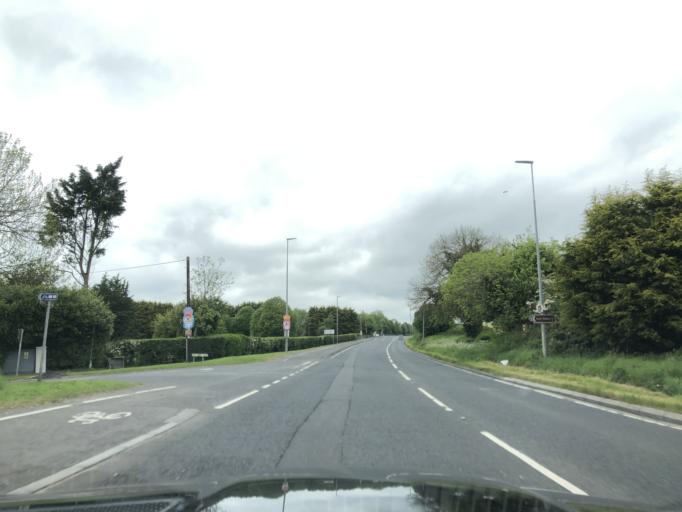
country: GB
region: Northern Ireland
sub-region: Down District
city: Downpatrick
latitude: 54.3421
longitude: -5.7307
